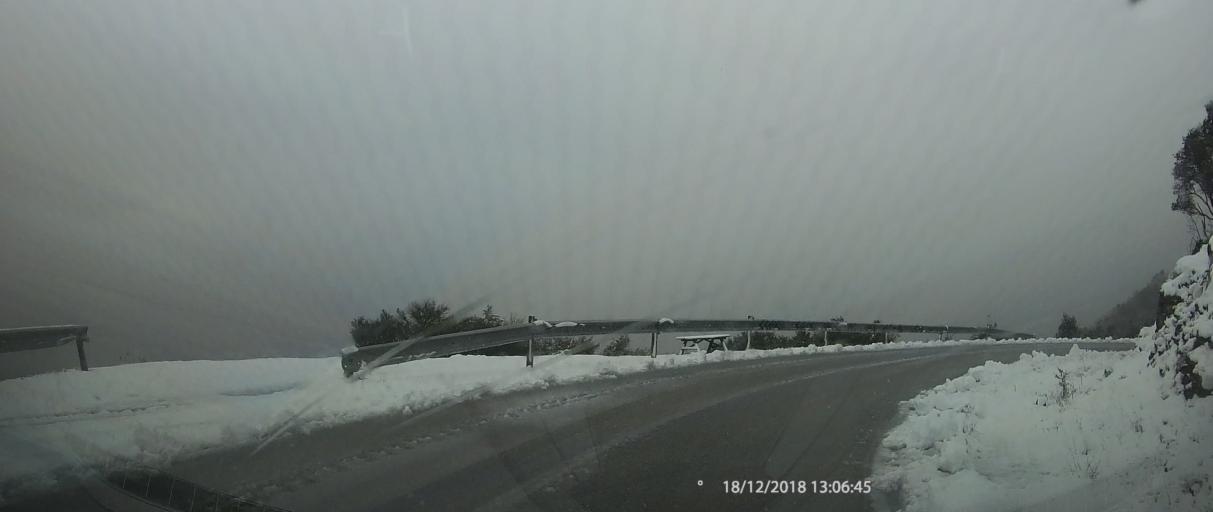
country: GR
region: Central Macedonia
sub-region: Nomos Pierias
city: Litochoro
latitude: 40.1096
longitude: 22.4752
